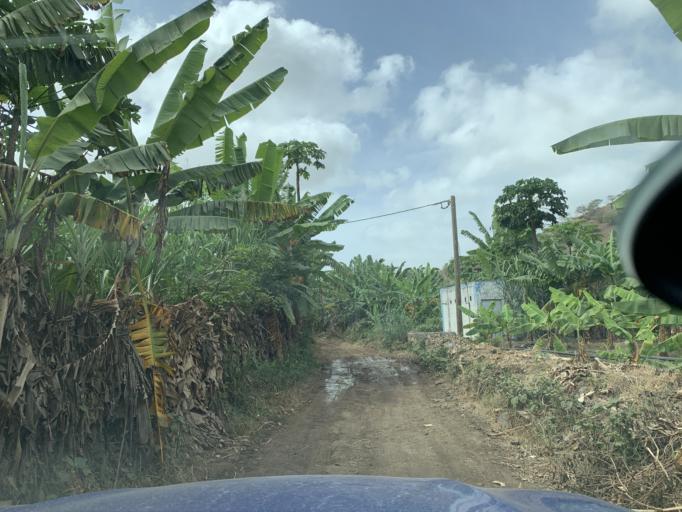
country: CV
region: Santa Cruz
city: Santa Cruz
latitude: 15.1128
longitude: -23.5652
